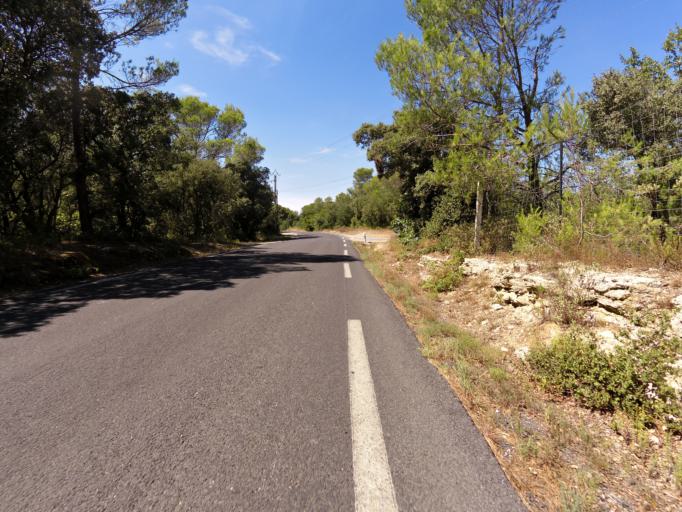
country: FR
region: Languedoc-Roussillon
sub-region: Departement de l'Herault
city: Boisseron
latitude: 43.7607
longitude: 4.1057
